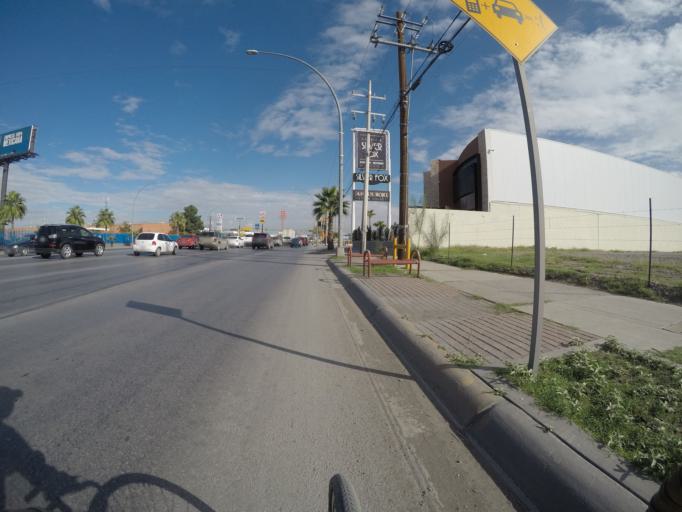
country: MX
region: Chihuahua
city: Ciudad Juarez
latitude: 31.7315
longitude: -106.4243
